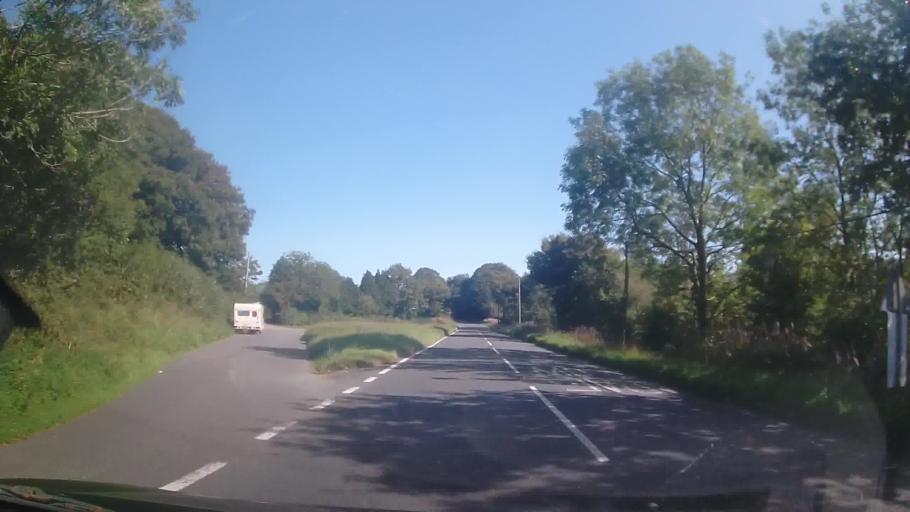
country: GB
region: Wales
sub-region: Sir Powys
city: Mochdre
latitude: 52.4804
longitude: -3.3368
